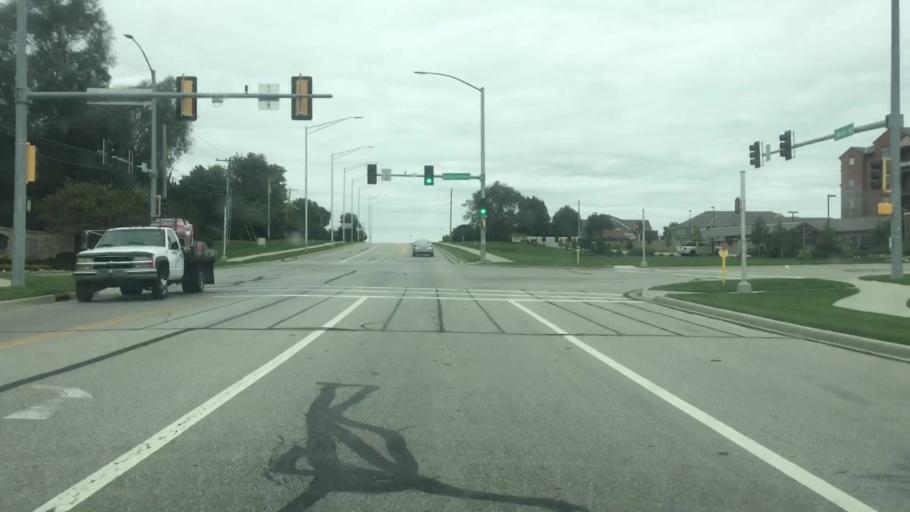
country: US
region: Kansas
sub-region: Johnson County
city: Lenexa
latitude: 38.9766
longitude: -94.7796
